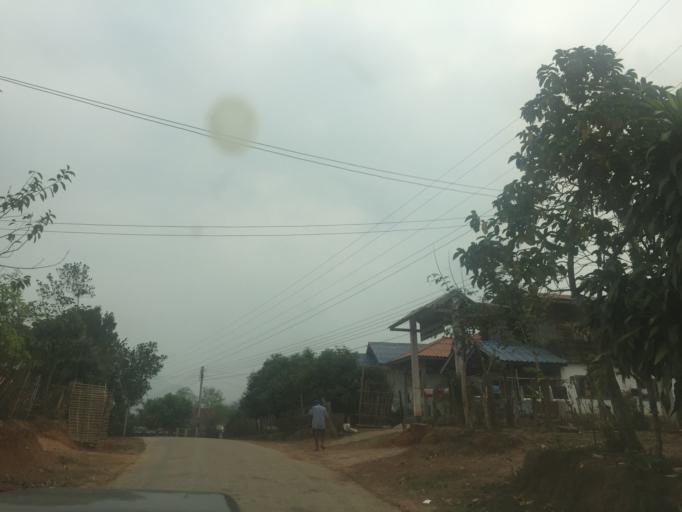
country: LA
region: Vientiane
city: Muang Sanakham
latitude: 18.3859
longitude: 101.5336
